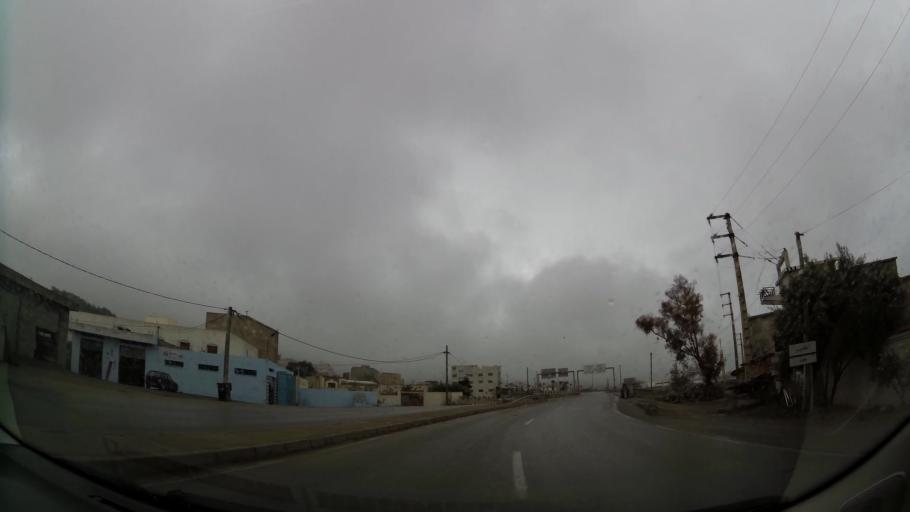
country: MA
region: Taza-Al Hoceima-Taounate
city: Imzourene
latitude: 35.1939
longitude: -3.8934
